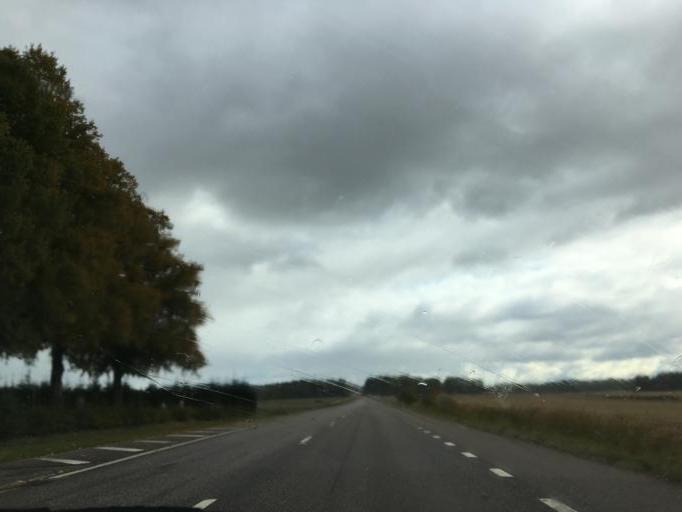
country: SE
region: Soedermanland
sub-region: Nykopings Kommun
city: Stigtomta
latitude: 58.7949
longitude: 16.7921
